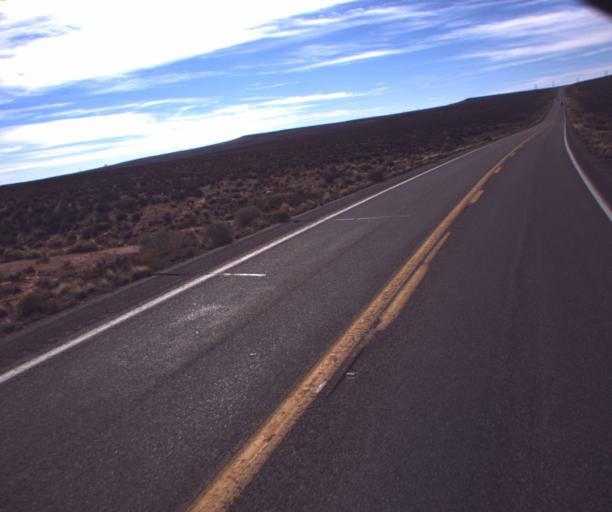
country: US
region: Arizona
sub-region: Coconino County
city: LeChee
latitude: 36.8266
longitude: -111.3096
